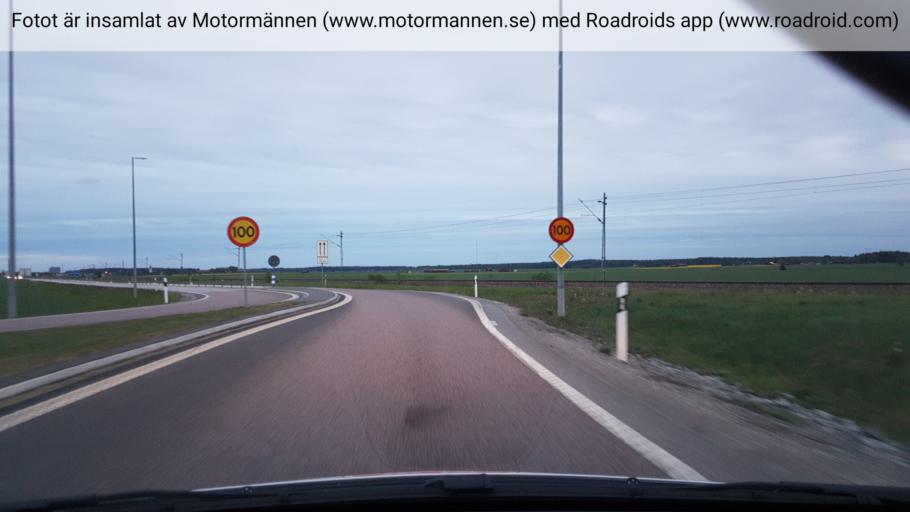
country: SE
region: Vaestmanland
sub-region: Sala Kommun
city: Sala
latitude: 59.8879
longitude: 16.6236
